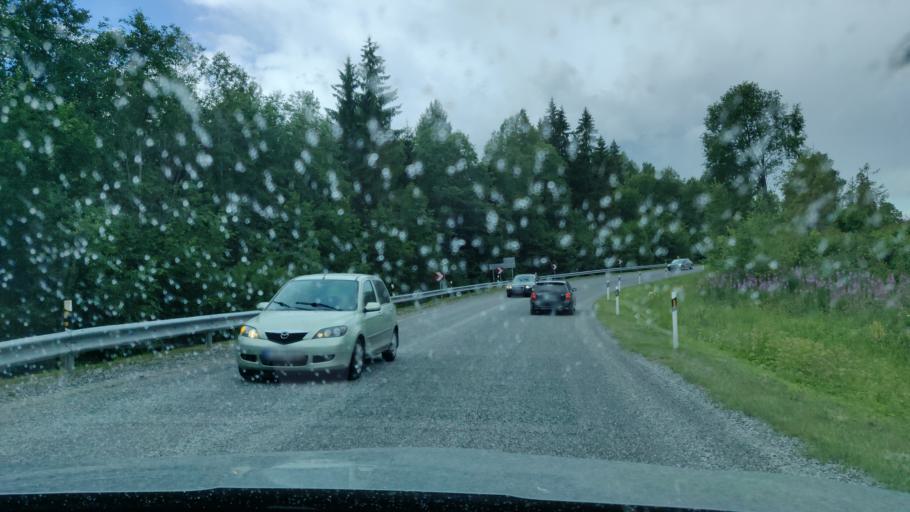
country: EE
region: Vorumaa
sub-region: Antsla vald
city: Vana-Antsla
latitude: 58.0225
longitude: 26.5806
